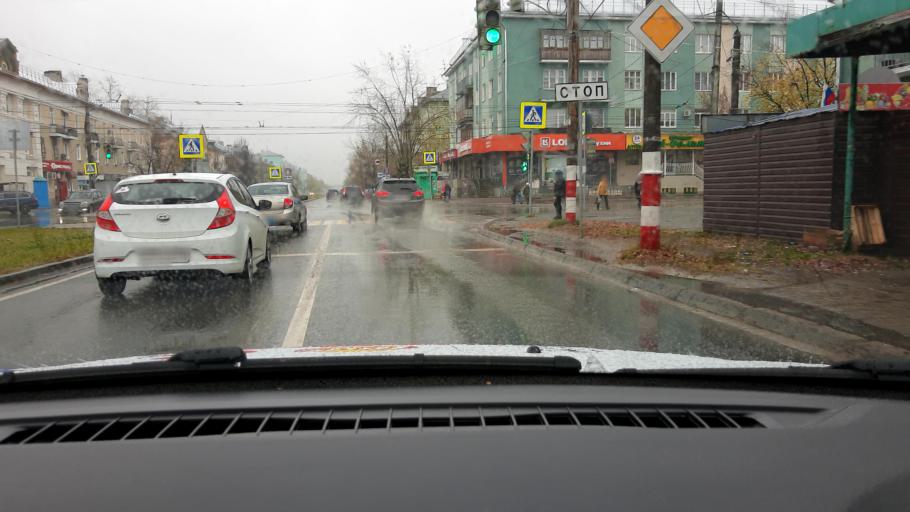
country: RU
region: Nizjnij Novgorod
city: Dzerzhinsk
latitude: 56.2436
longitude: 43.4396
